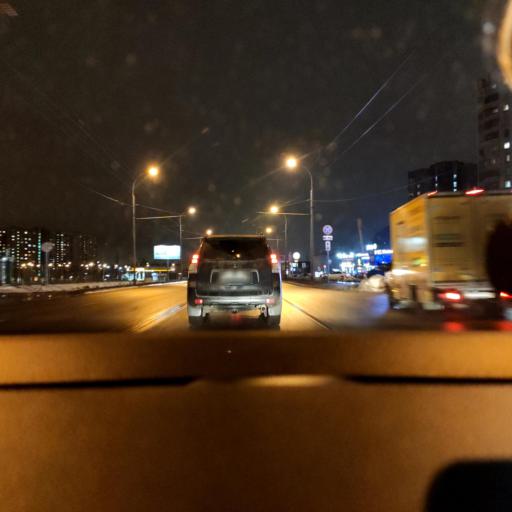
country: RU
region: Moskovskaya
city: Reutov
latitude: 55.7449
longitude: 37.8603
